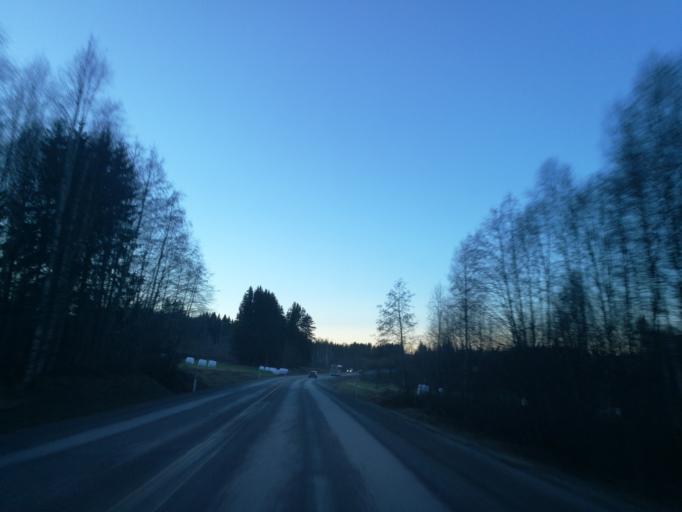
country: NO
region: Hedmark
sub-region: Eidskog
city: Skotterud
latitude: 59.9743
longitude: 12.1327
